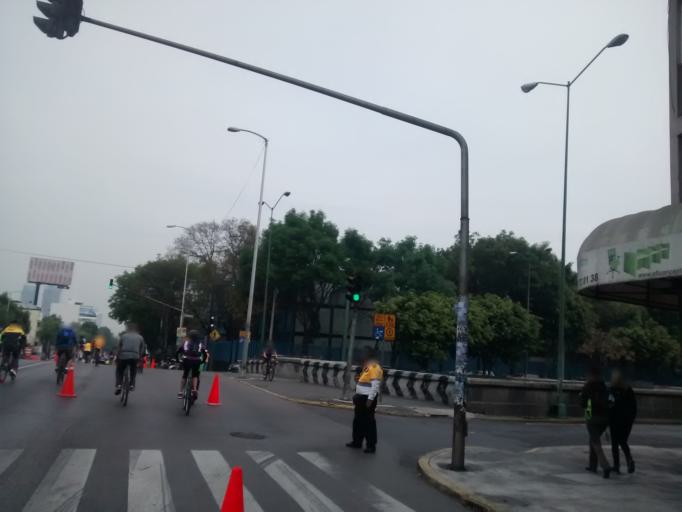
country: MX
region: Mexico City
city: Colonia del Valle
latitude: 19.3994
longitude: -99.1801
